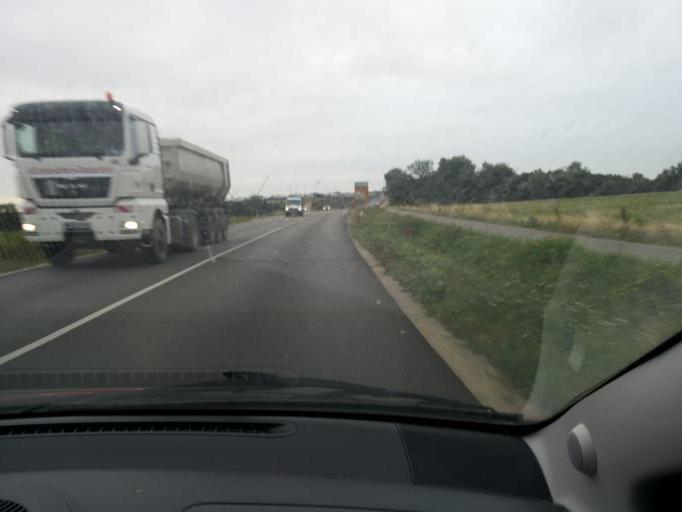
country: DE
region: Bavaria
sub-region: Upper Bavaria
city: Gaimersheim
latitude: 48.7877
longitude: 11.3870
